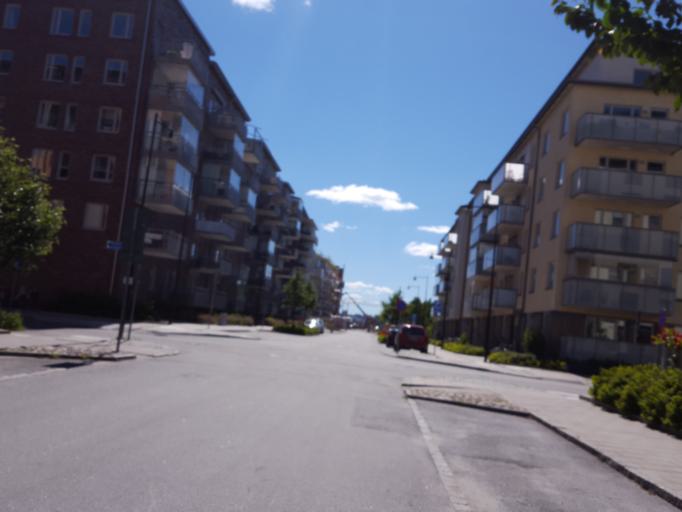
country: SE
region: Uppsala
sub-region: Uppsala Kommun
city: Uppsala
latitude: 59.8498
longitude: 17.6542
